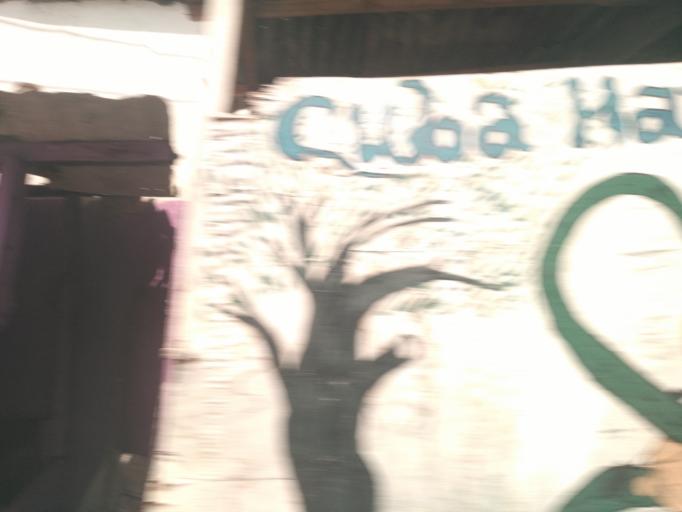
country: TZ
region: Dar es Salaam
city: Magomeni
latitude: -6.7689
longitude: 39.2607
